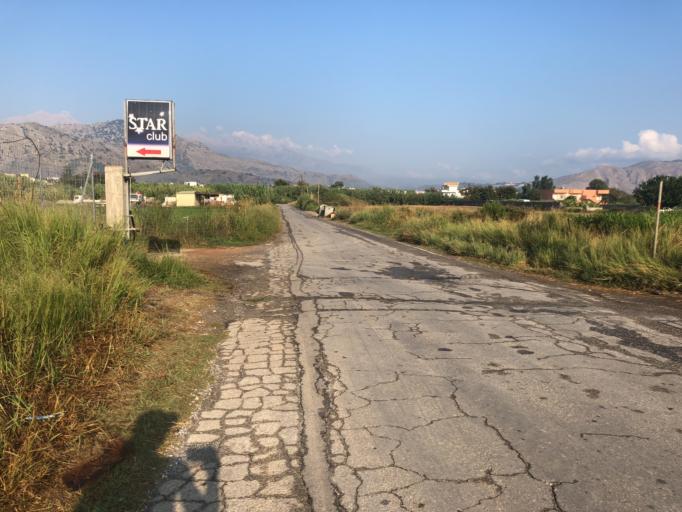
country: GR
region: Crete
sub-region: Nomos Chanias
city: Georgioupolis
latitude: 35.3482
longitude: 24.3056
